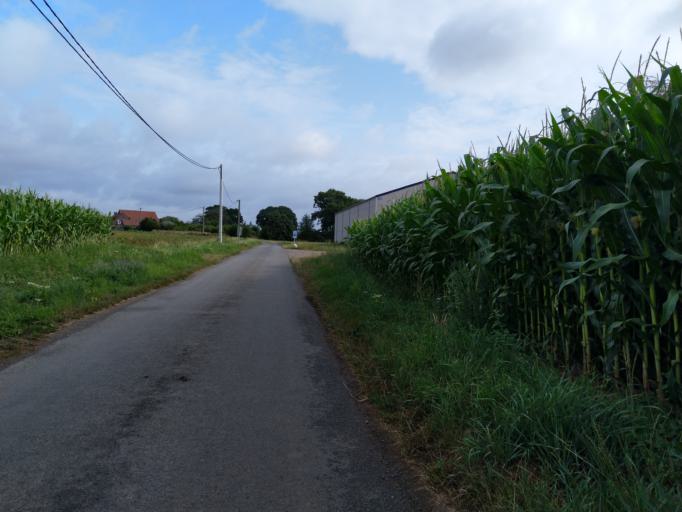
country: BE
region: Wallonia
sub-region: Province du Hainaut
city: Lens
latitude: 50.5356
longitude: 3.8826
